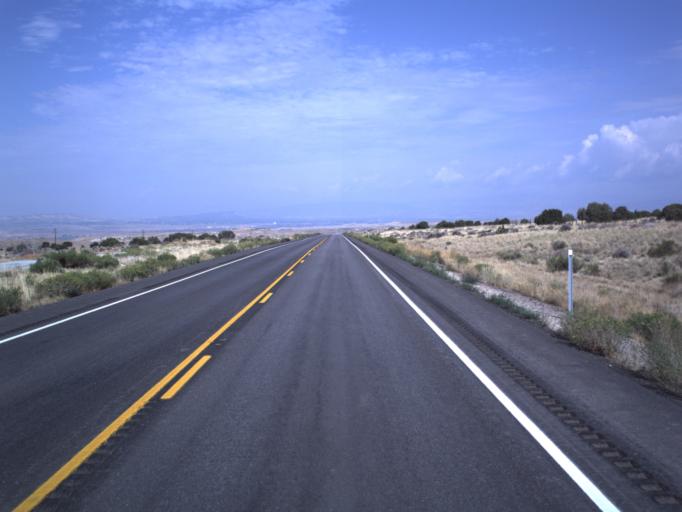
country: US
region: Utah
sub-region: Uintah County
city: Naples
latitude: 40.3242
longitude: -109.2652
